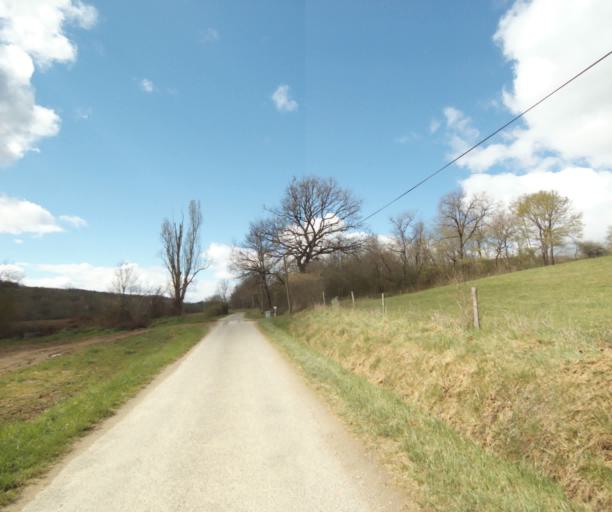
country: FR
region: Midi-Pyrenees
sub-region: Departement de l'Ariege
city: Saverdun
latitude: 43.1914
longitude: 1.5640
